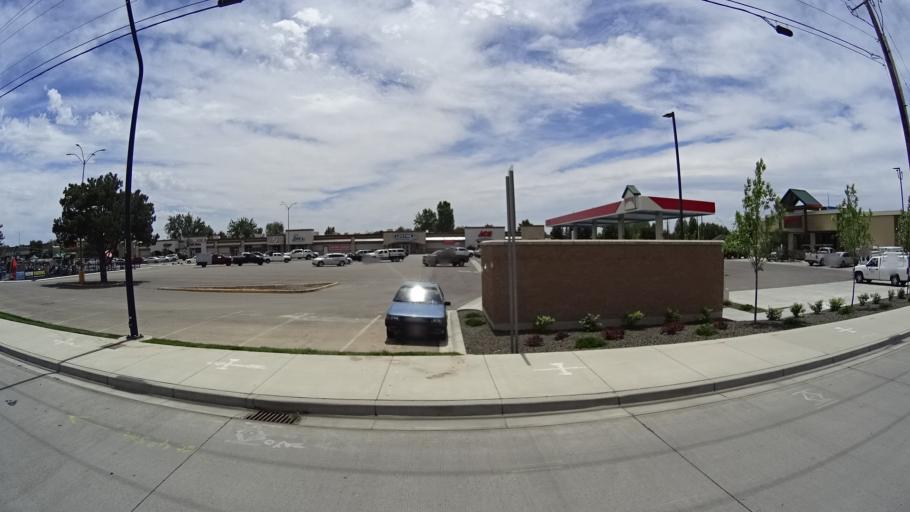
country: US
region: Idaho
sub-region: Ada County
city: Garden City
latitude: 43.6194
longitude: -116.3133
